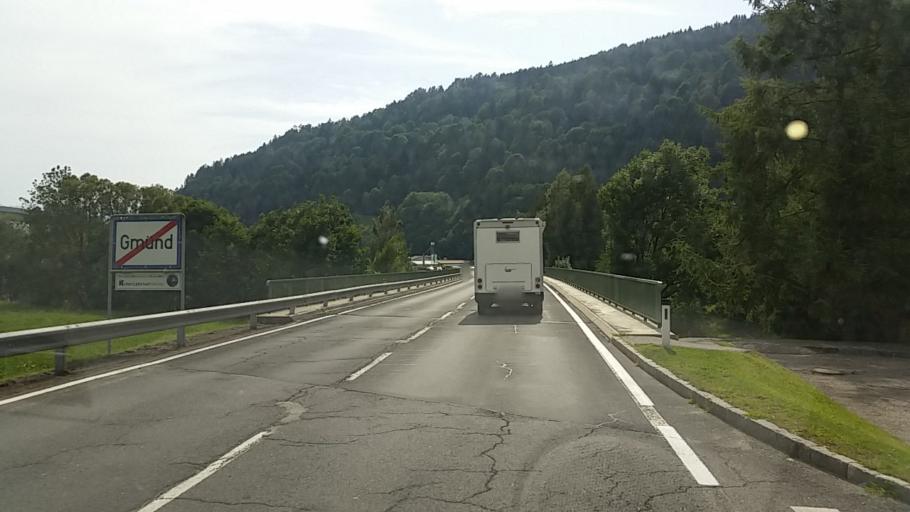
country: AT
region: Carinthia
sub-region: Politischer Bezirk Spittal an der Drau
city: Gmuend
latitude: 46.9050
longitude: 13.5343
